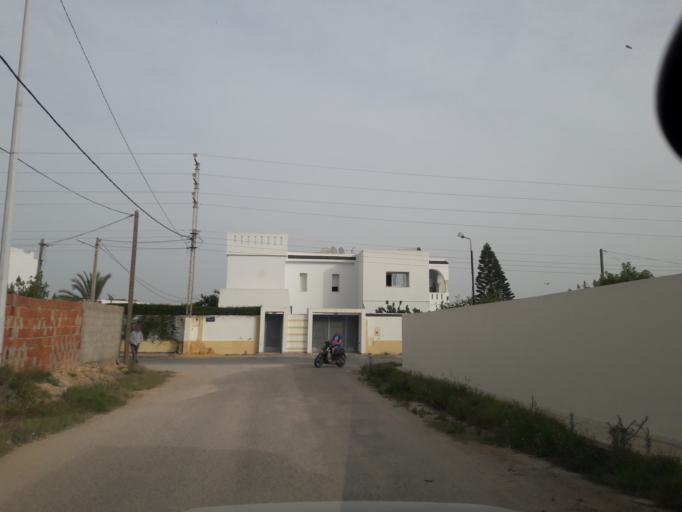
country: TN
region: Safaqis
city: Al Qarmadah
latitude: 34.7770
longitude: 10.7694
